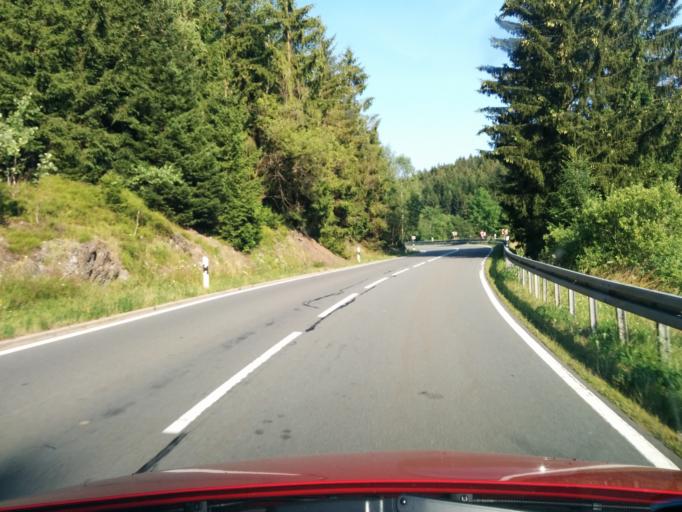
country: DE
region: Saxony-Anhalt
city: Benneckenstein
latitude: 51.6986
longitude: 10.6736
